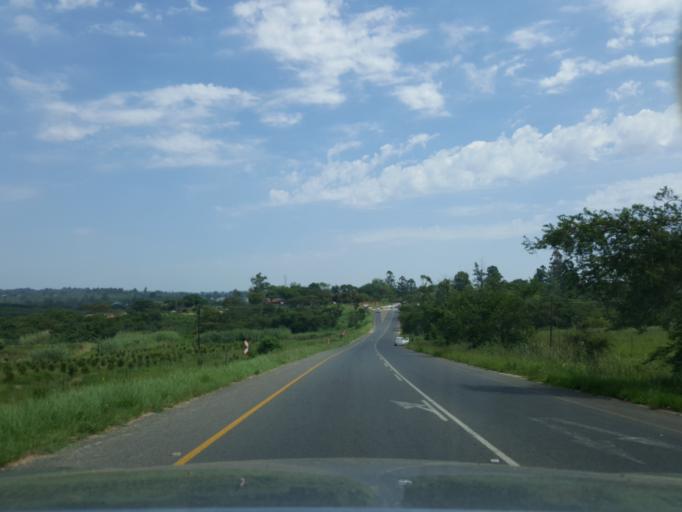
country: ZA
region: Mpumalanga
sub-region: Ehlanzeni District
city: White River
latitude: -25.3577
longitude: 31.0715
